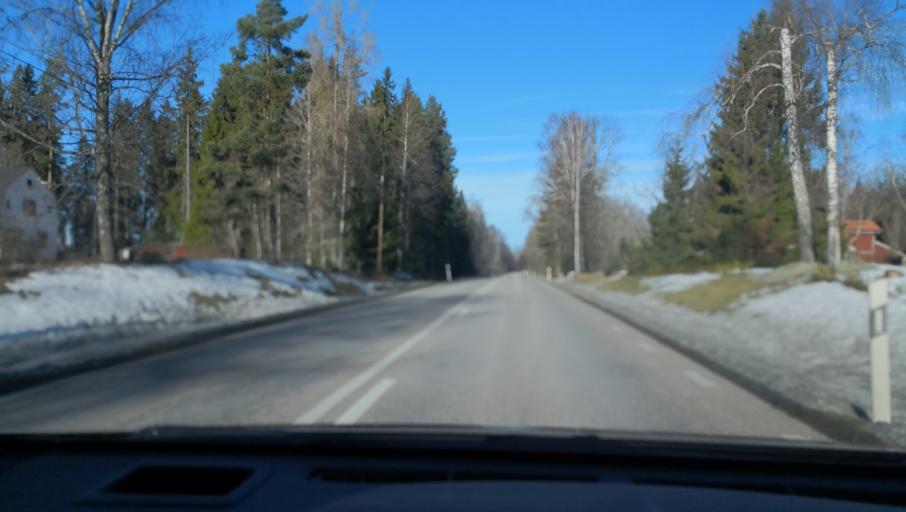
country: SE
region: Uppsala
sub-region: Osthammars Kommun
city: Osterbybruk
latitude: 60.1725
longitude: 17.8491
